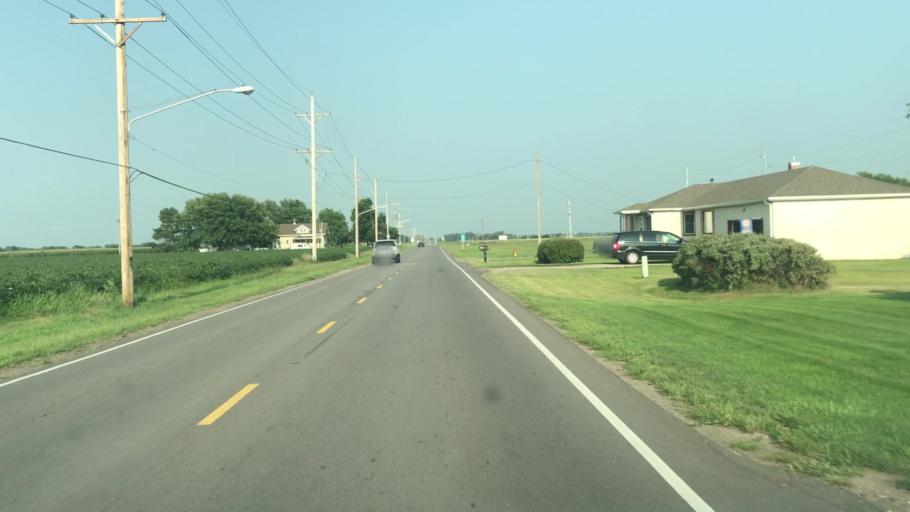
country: US
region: Nebraska
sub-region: Hall County
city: Grand Island
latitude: 40.9455
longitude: -98.3237
